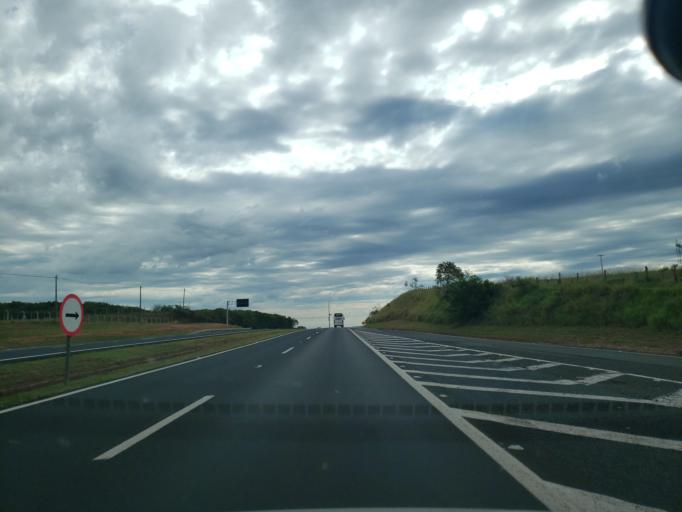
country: BR
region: Sao Paulo
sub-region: Bauru
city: Bauru
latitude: -22.2727
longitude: -49.0969
